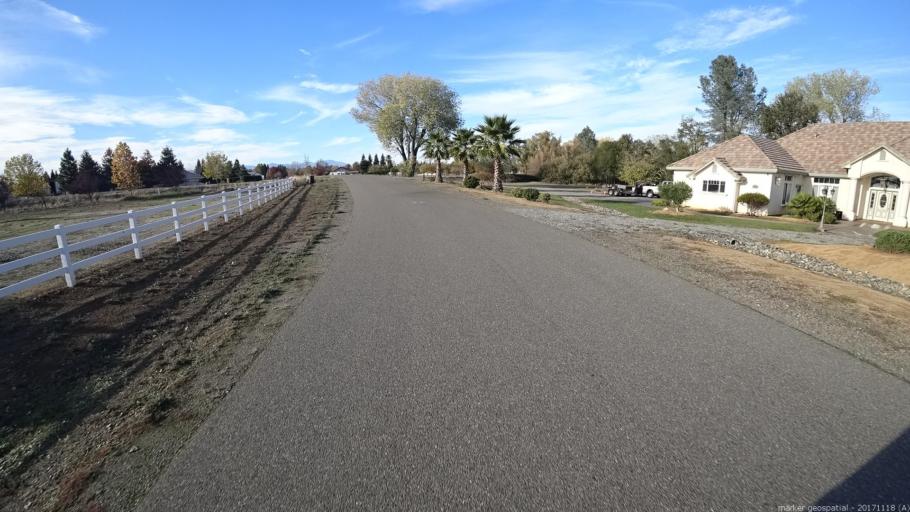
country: US
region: California
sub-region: Shasta County
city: Cottonwood
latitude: 40.3771
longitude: -122.3330
